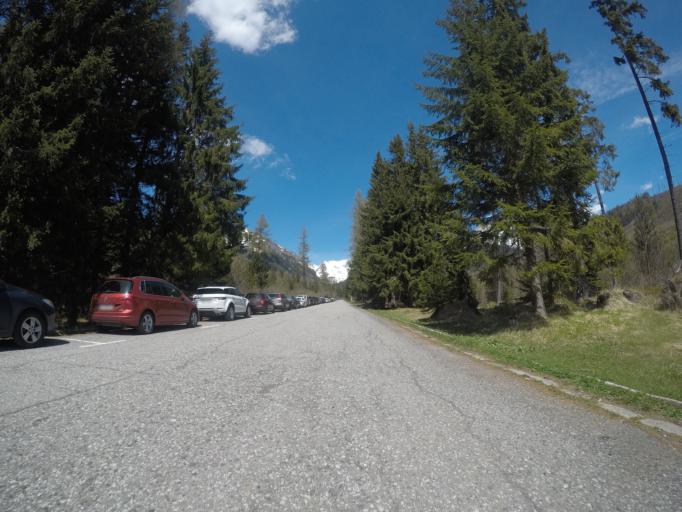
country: SK
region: Presovsky
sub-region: Okres Poprad
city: Strba
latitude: 49.1239
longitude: 20.0748
